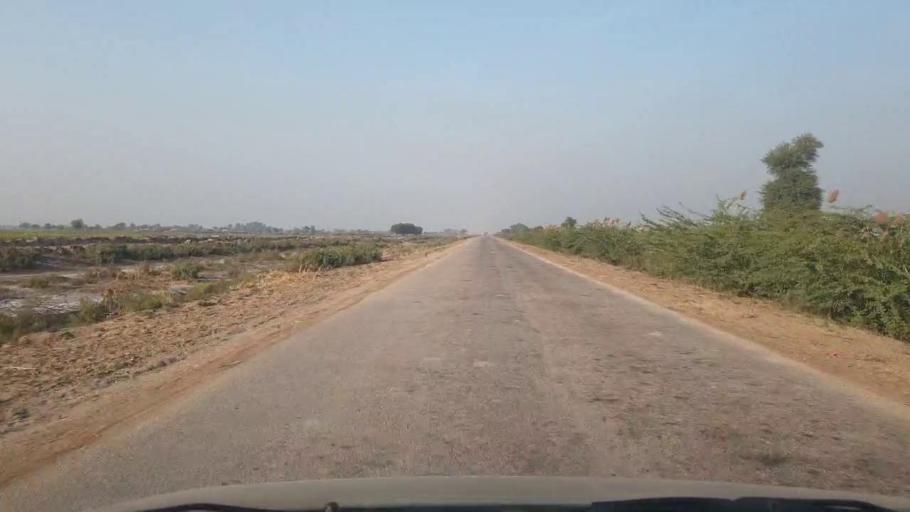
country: PK
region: Sindh
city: Mirwah Gorchani
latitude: 25.3340
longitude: 69.1675
